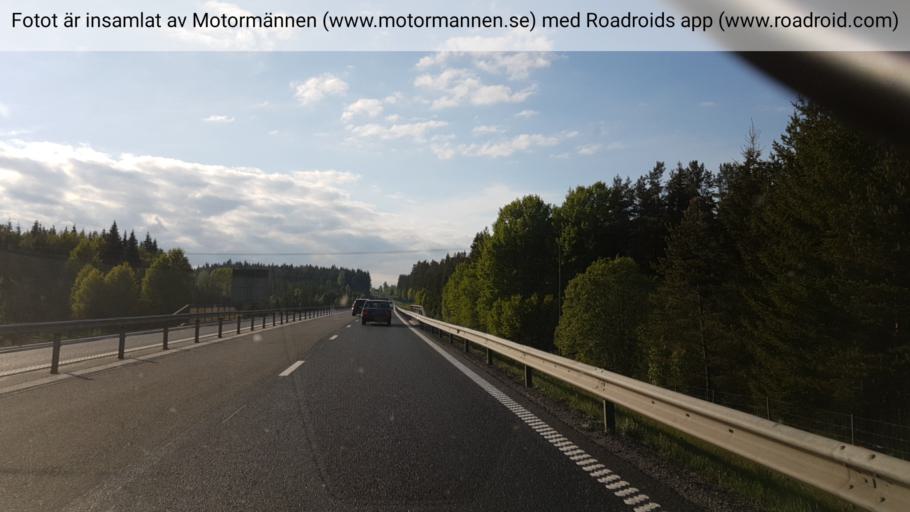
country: SE
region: Joenkoeping
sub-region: Nassjo Kommun
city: Malmback
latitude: 57.6935
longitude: 14.4487
